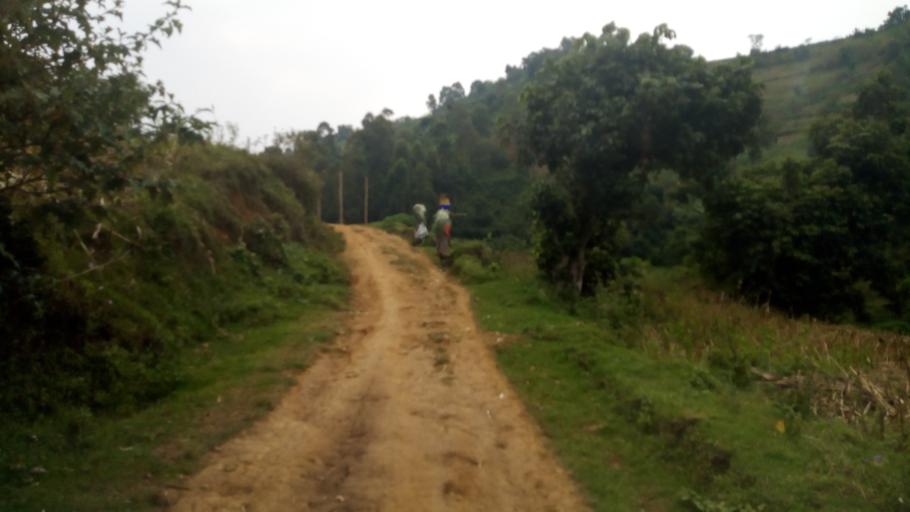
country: UG
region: Western Region
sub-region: Kisoro District
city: Kisoro
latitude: -1.2463
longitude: 29.6210
